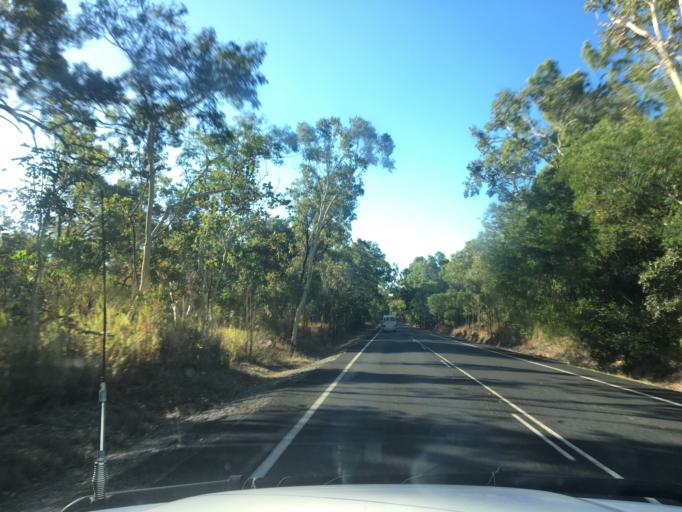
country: AU
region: Queensland
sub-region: Cairns
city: Palm Cove
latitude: -16.6716
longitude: 145.5680
